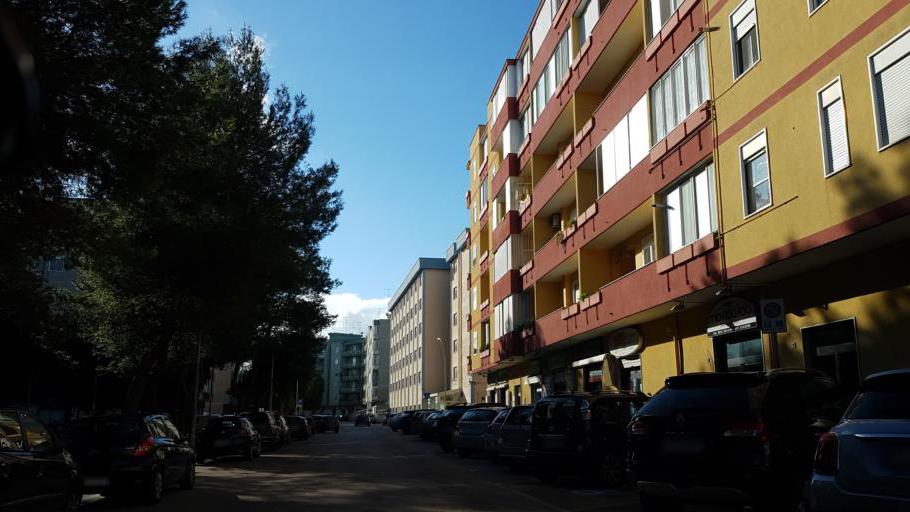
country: IT
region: Apulia
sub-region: Provincia di Brindisi
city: Brindisi
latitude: 40.6268
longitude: 17.9244
